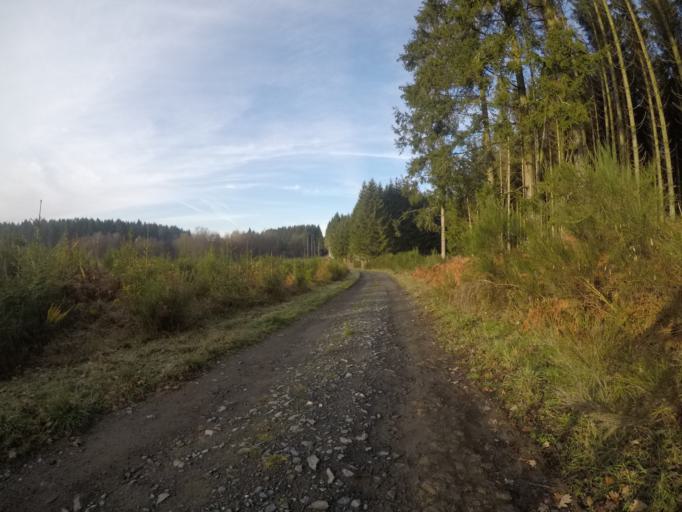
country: BE
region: Wallonia
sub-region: Province du Luxembourg
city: Habay-la-Vieille
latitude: 49.7737
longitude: 5.6380
